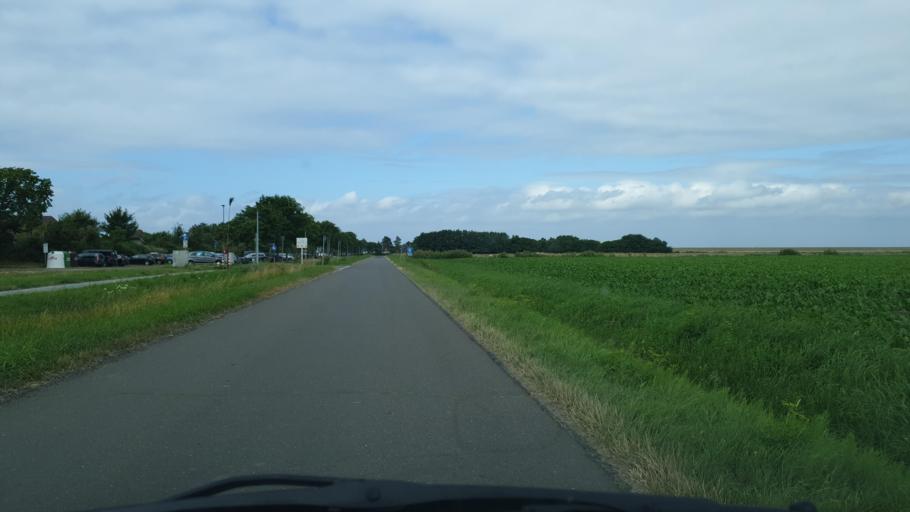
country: DE
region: Schleswig-Holstein
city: Friedrichskoog
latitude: 54.0336
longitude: 8.8490
